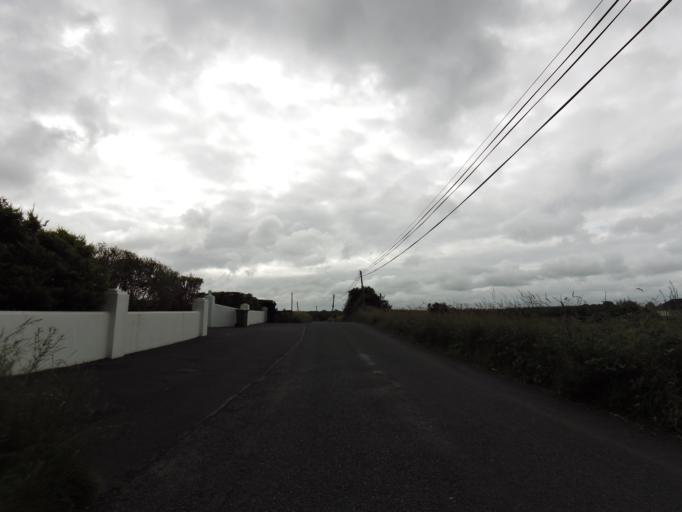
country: IE
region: Connaught
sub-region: County Galway
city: Athenry
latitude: 53.2922
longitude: -8.7035
